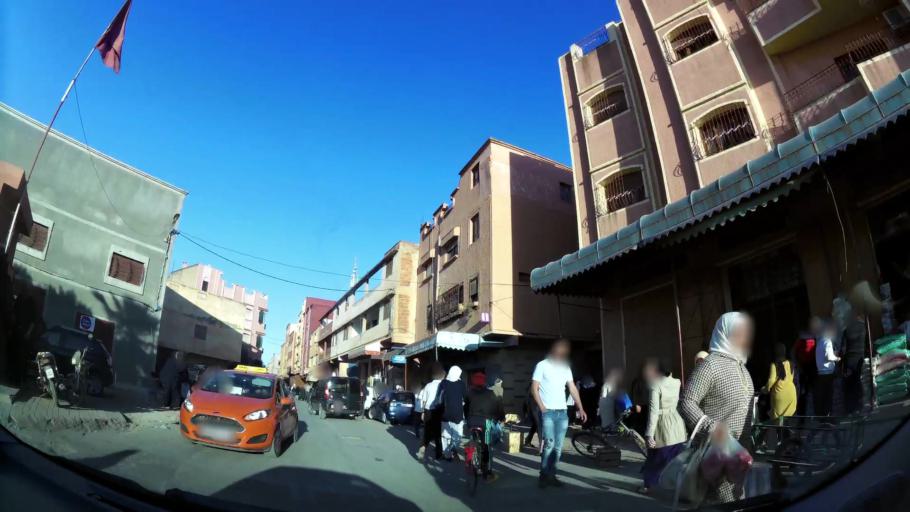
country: MA
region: Oriental
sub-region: Berkane-Taourirt
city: Berkane
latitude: 34.9218
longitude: -2.3168
